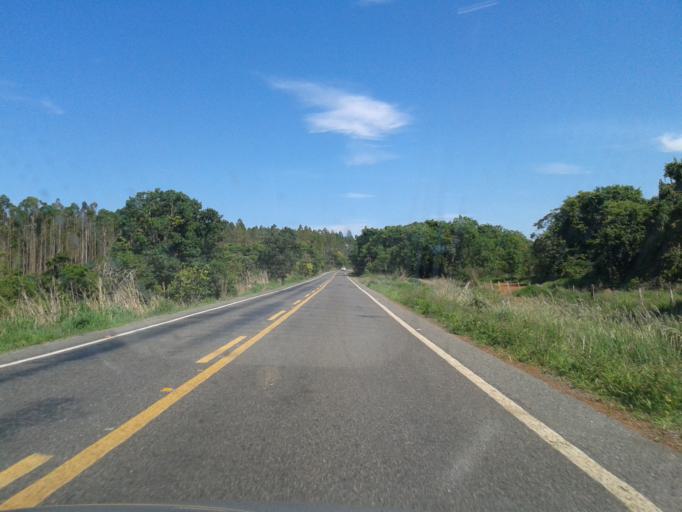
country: BR
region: Goias
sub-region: Piracanjuba
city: Piracanjuba
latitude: -17.3313
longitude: -48.7993
